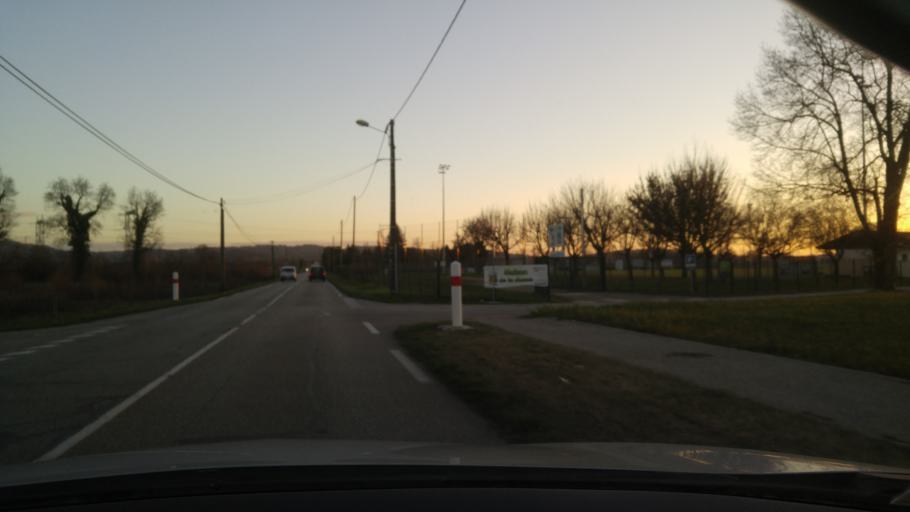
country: FR
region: Rhone-Alpes
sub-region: Departement de l'Isere
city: Tignieu-Jameyzieu
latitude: 45.7278
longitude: 5.1872
